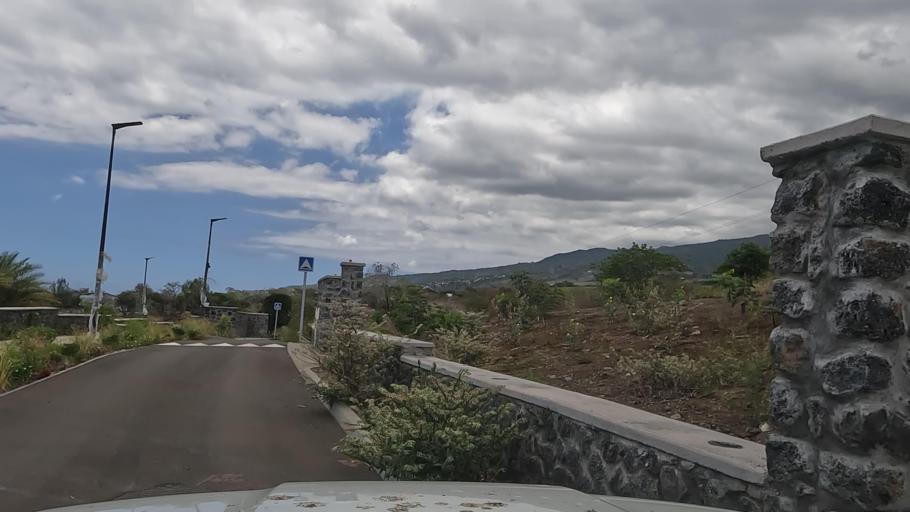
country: RE
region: Reunion
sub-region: Reunion
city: Saint-Louis
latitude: -21.2664
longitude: 55.4156
